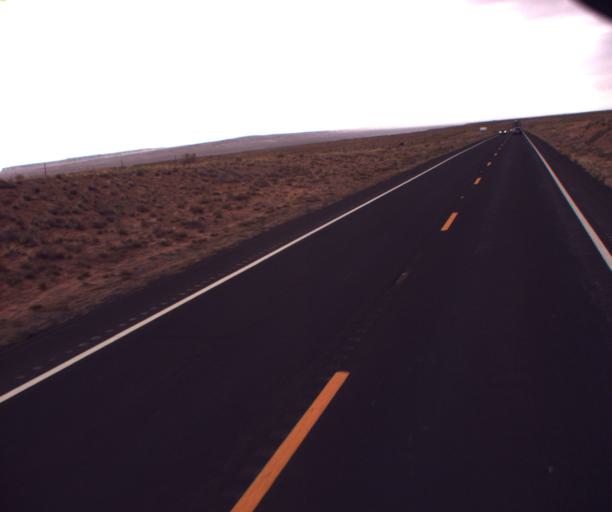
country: US
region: Arizona
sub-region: Coconino County
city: Tuba City
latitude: 36.1908
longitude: -111.0673
